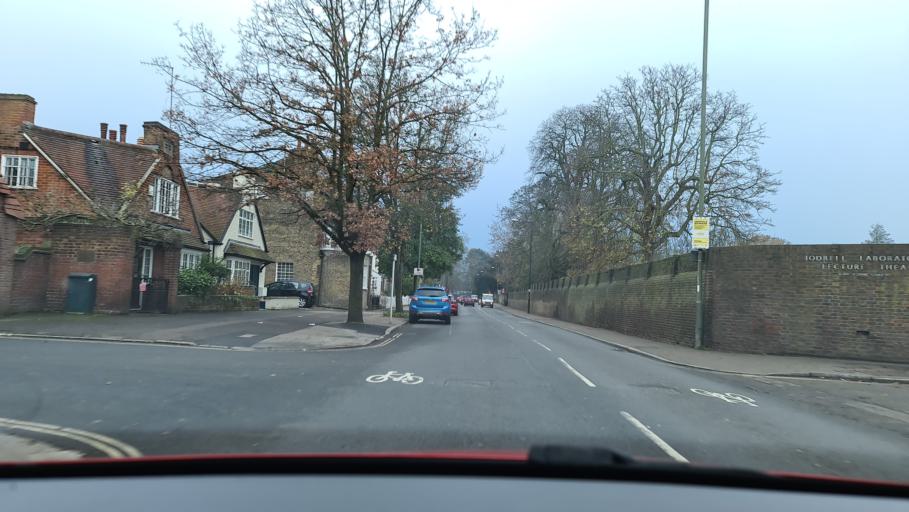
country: GB
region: England
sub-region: Greater London
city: Brentford
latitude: 51.4819
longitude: -0.2876
